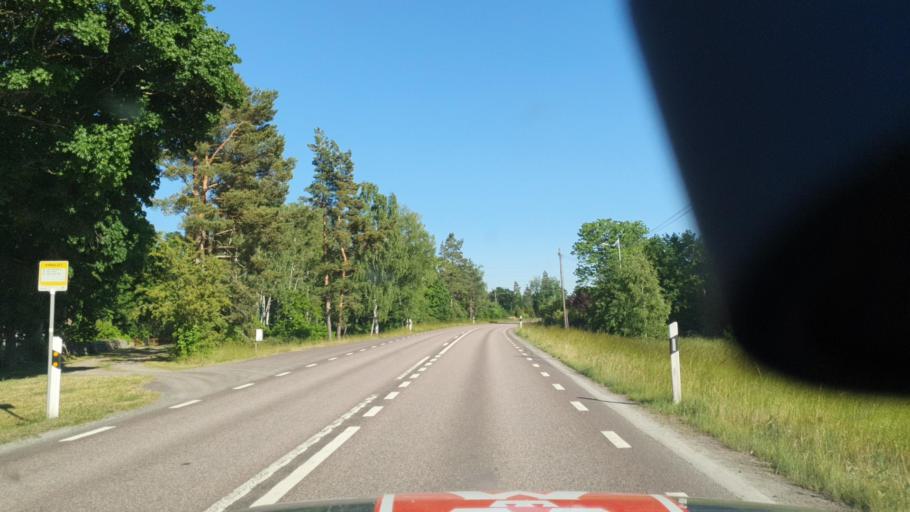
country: SE
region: Kalmar
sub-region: Nybro Kommun
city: Nybro
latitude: 56.7703
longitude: 15.8599
